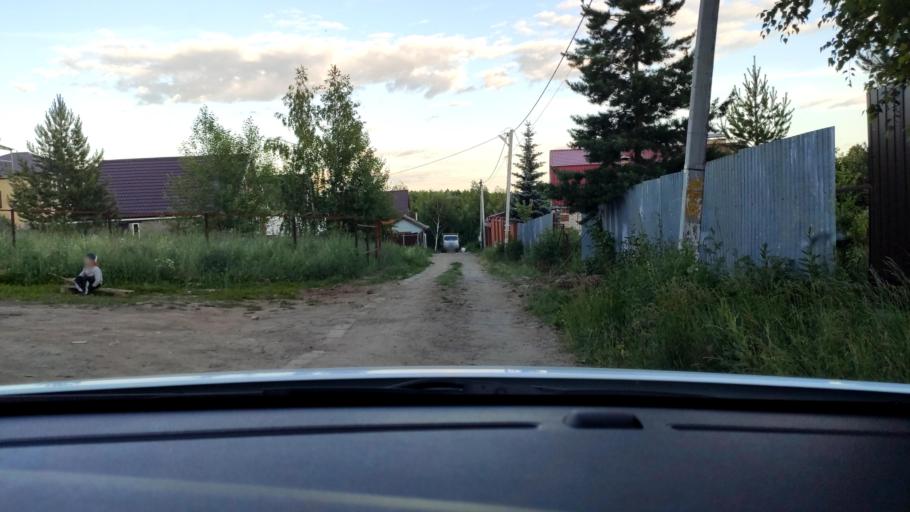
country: RU
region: Tatarstan
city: Stolbishchi
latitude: 55.7594
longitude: 49.3032
